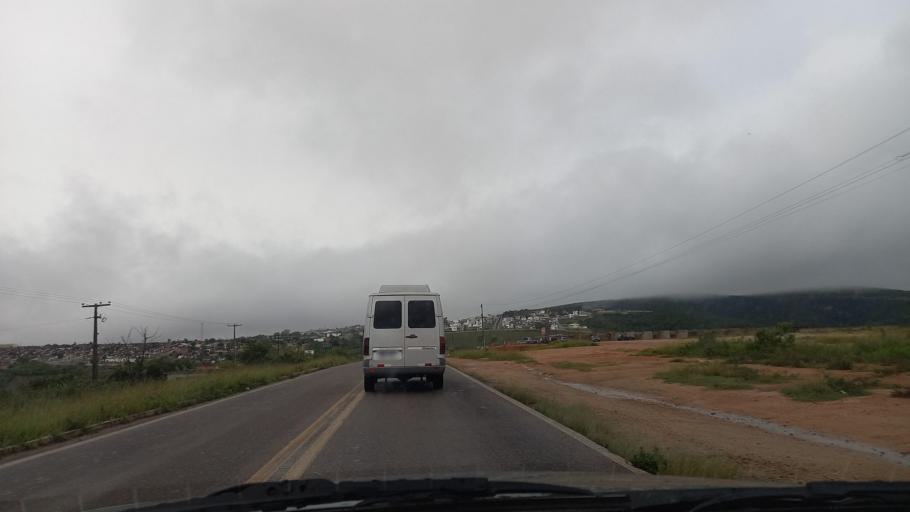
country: BR
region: Pernambuco
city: Garanhuns
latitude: -8.8572
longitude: -36.5121
